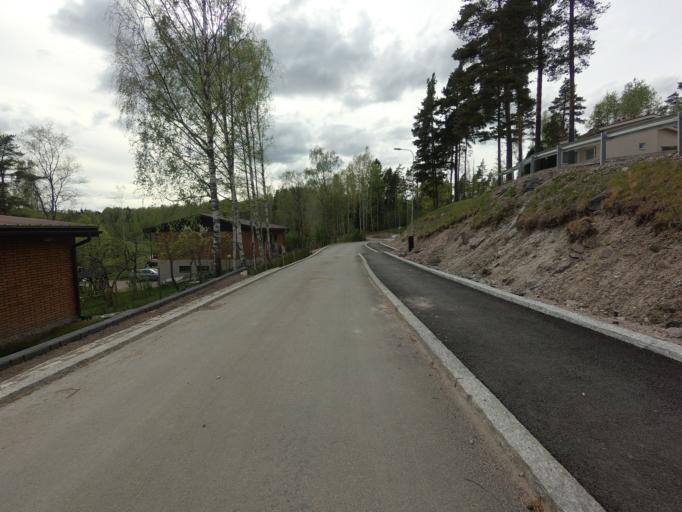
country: FI
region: Uusimaa
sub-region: Helsinki
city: Kauniainen
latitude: 60.1889
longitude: 24.7227
